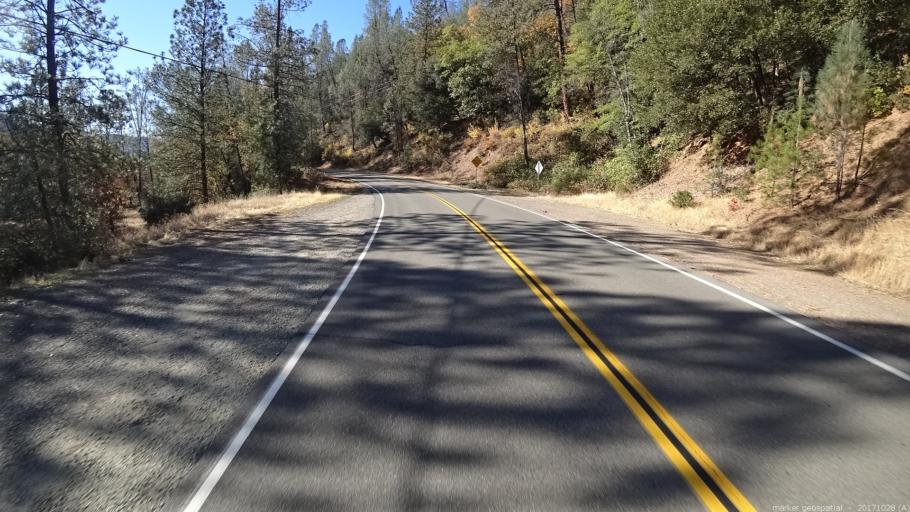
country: US
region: California
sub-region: Trinity County
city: Lewiston
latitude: 40.7462
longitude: -122.6253
